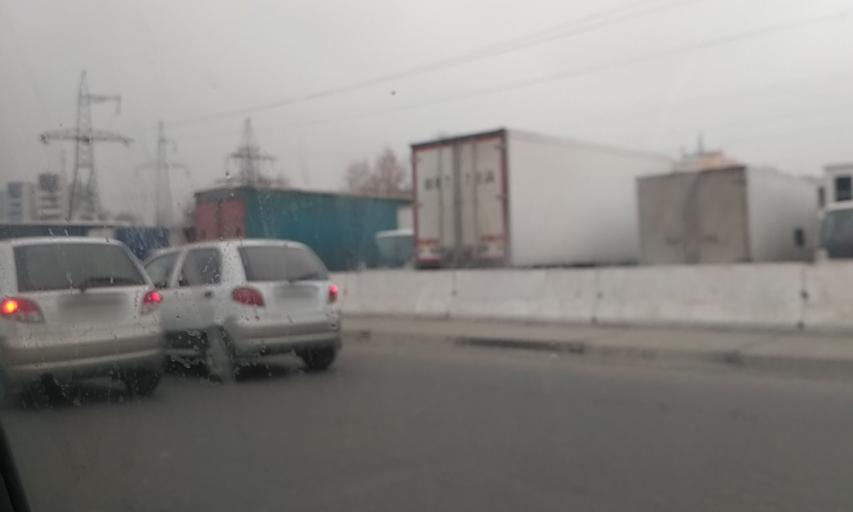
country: UZ
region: Toshkent Shahri
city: Tashkent
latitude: 41.2549
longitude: 69.1577
